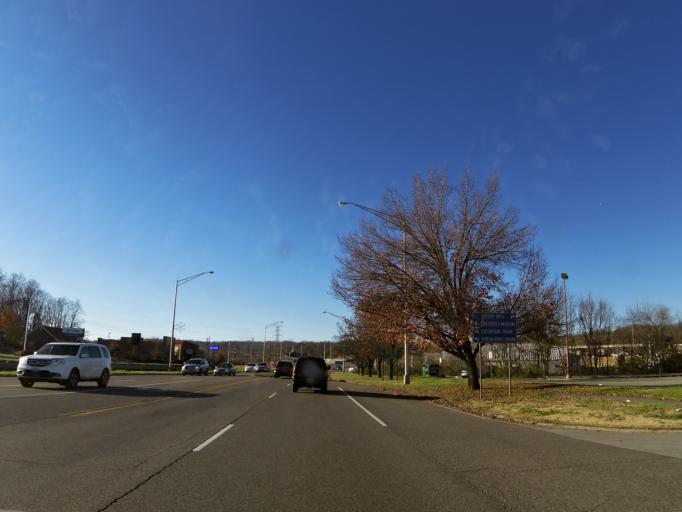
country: US
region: Tennessee
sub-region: Anderson County
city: Oak Ridge
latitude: 36.0091
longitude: -84.2669
